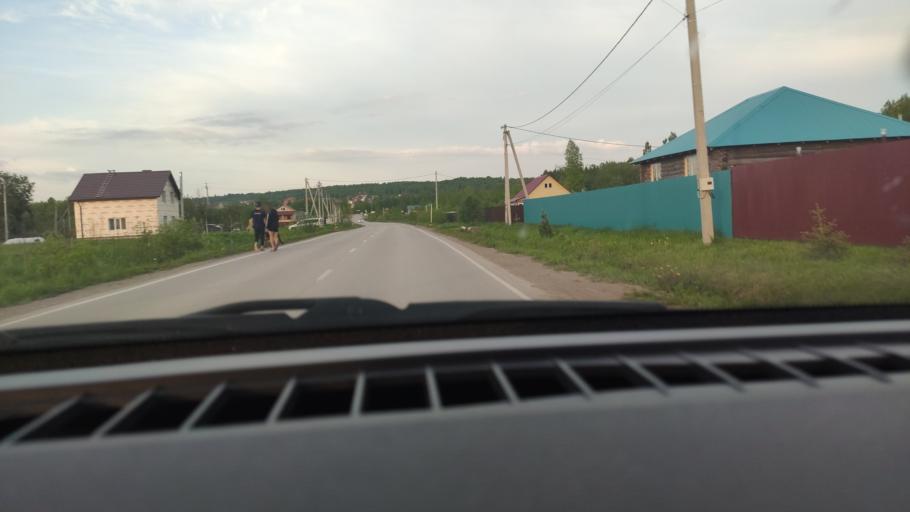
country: RU
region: Perm
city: Overyata
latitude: 58.0787
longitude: 55.9929
